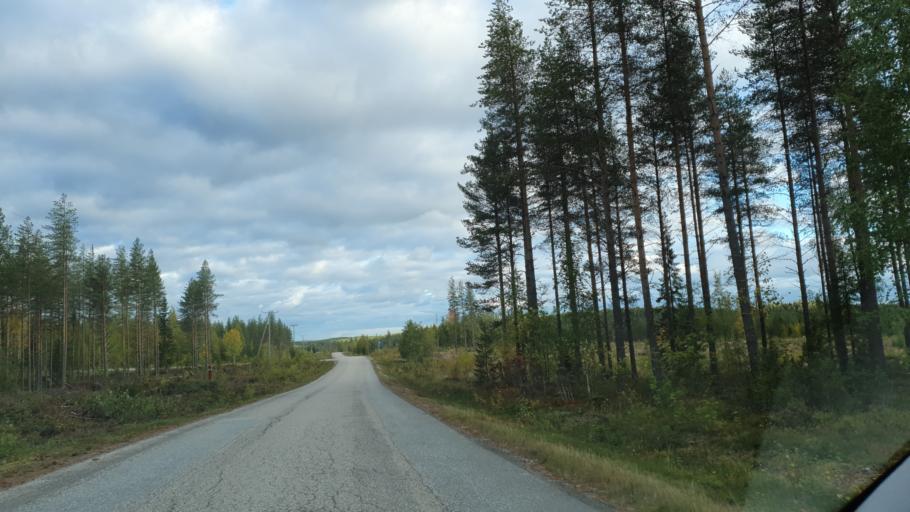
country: FI
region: North Karelia
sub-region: Pielisen Karjala
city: Lieksa
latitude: 63.9205
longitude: 30.1581
